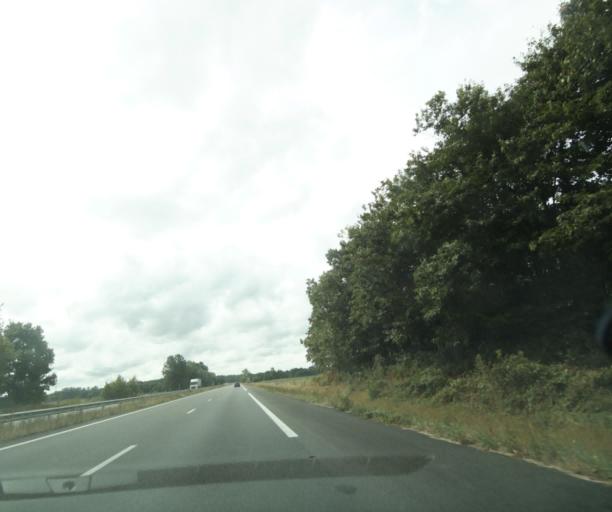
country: FR
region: Poitou-Charentes
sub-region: Departement de la Charente-Maritime
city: Saint-Genis-de-Saintonge
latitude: 45.4858
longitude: -0.6167
